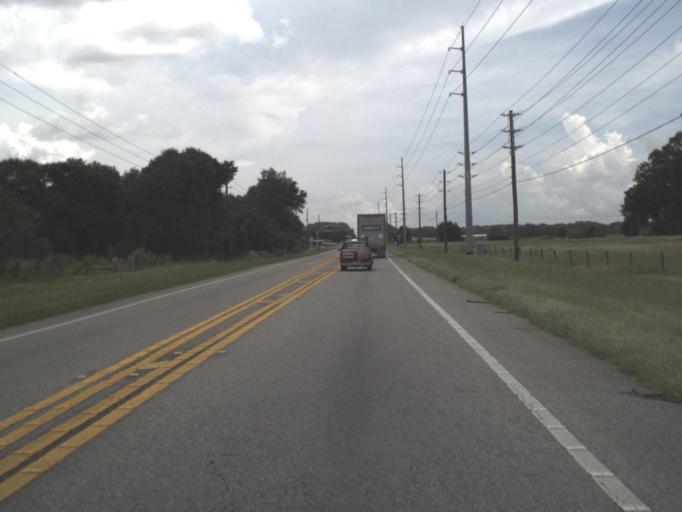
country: US
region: Florida
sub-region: Pasco County
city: San Antonio
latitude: 28.3242
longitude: -82.3619
